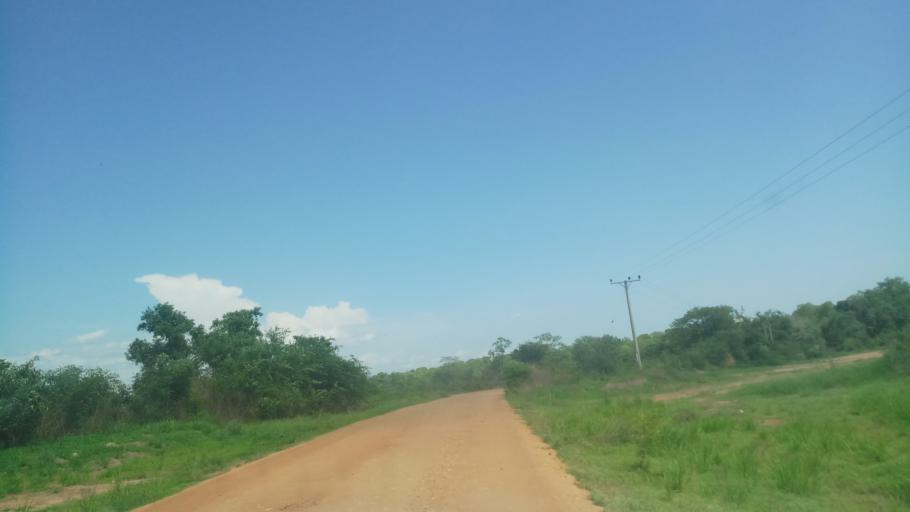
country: ET
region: Gambela
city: Gambela
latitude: 8.2200
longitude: 34.5640
